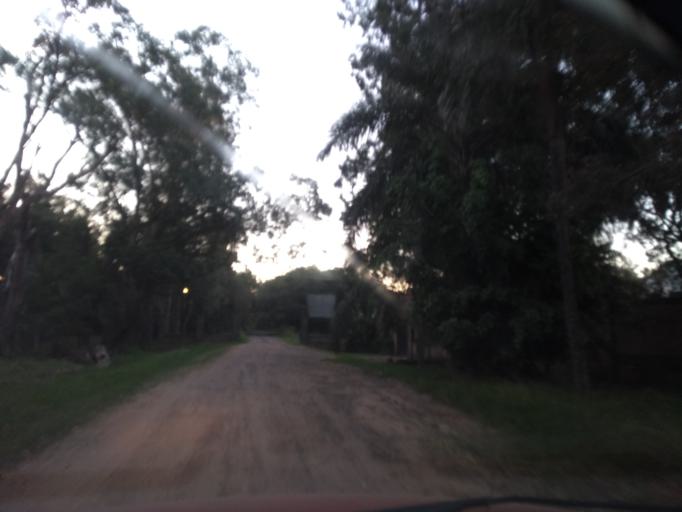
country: AR
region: Chaco
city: Fontana
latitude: -27.4221
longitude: -59.0048
